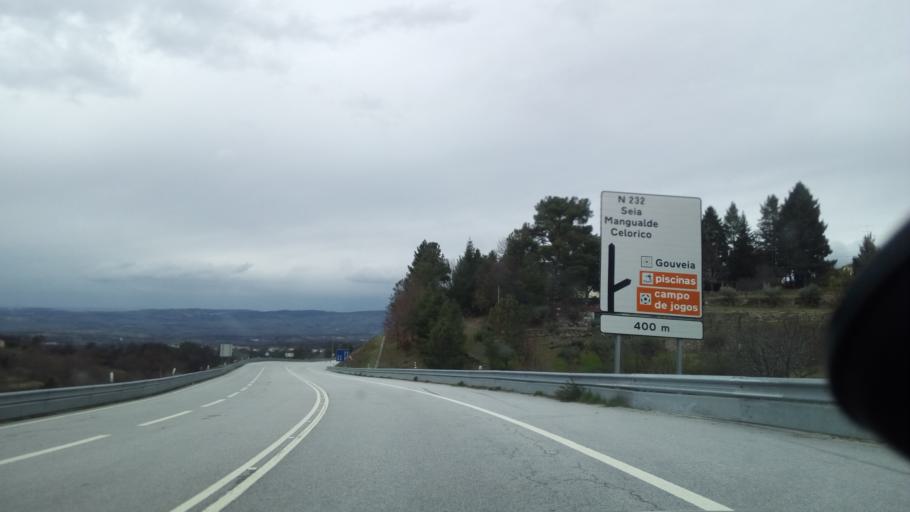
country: PT
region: Guarda
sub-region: Manteigas
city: Manteigas
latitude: 40.4817
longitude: -7.5966
